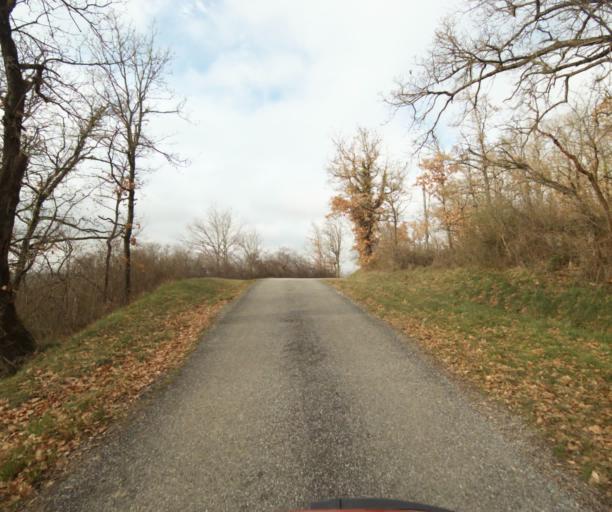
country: FR
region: Languedoc-Roussillon
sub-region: Departement de l'Aude
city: Belpech
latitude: 43.1678
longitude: 1.7379
